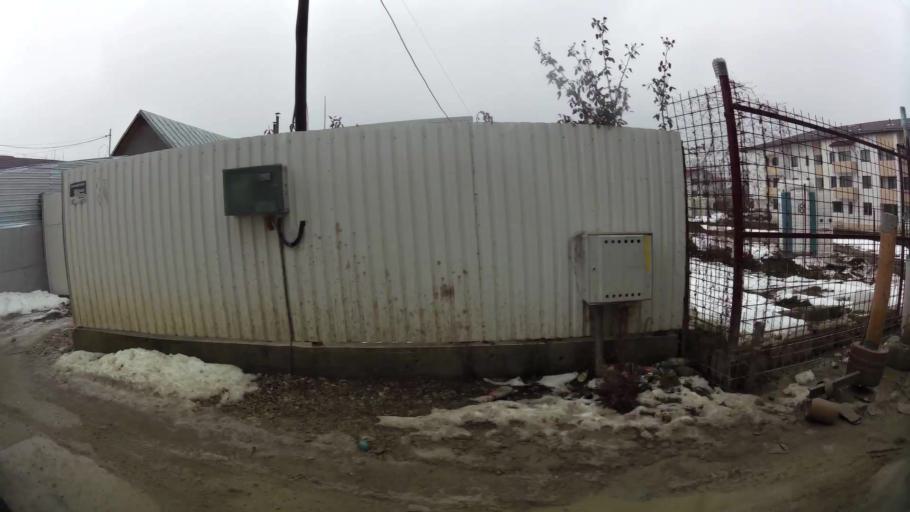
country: RO
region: Ilfov
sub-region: Comuna Popesti-Leordeni
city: Popesti-Leordeni
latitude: 44.4051
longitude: 26.1668
